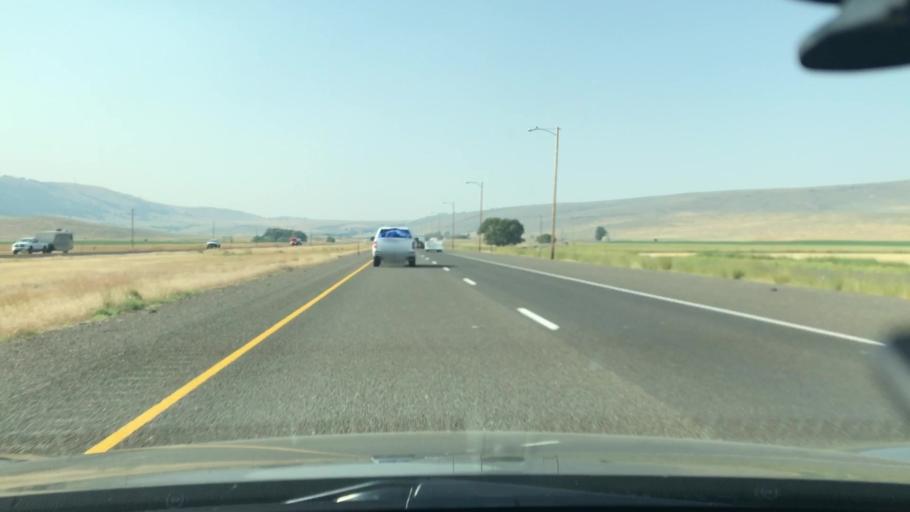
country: US
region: Oregon
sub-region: Union County
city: Union
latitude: 45.1100
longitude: -117.9572
